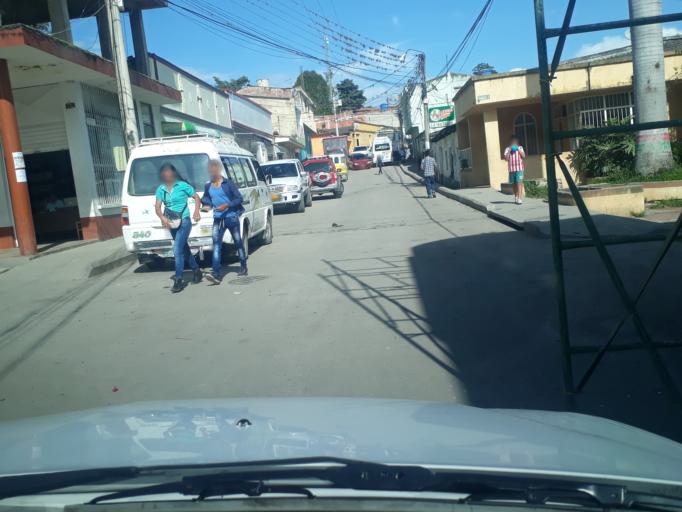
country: CO
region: Santander
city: Velez
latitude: 6.0624
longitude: -73.6371
